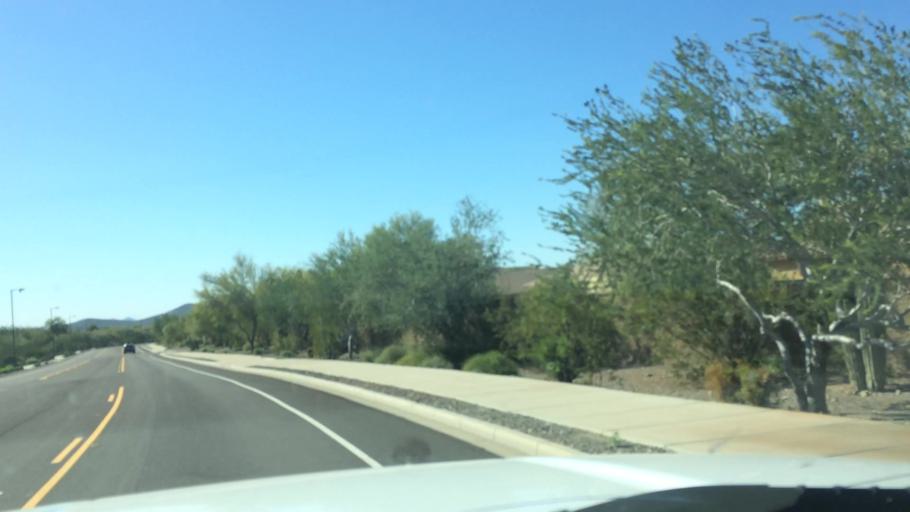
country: US
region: Arizona
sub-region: Maricopa County
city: Anthem
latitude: 33.8506
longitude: -112.1106
